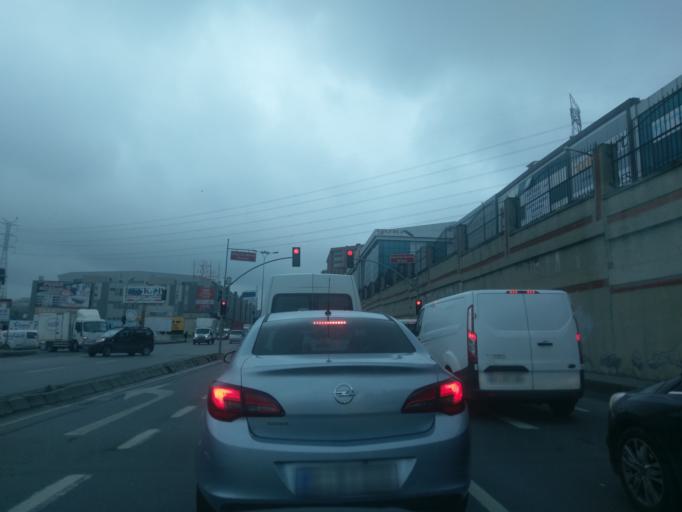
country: TR
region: Istanbul
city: Basaksehir
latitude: 41.0686
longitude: 28.7975
